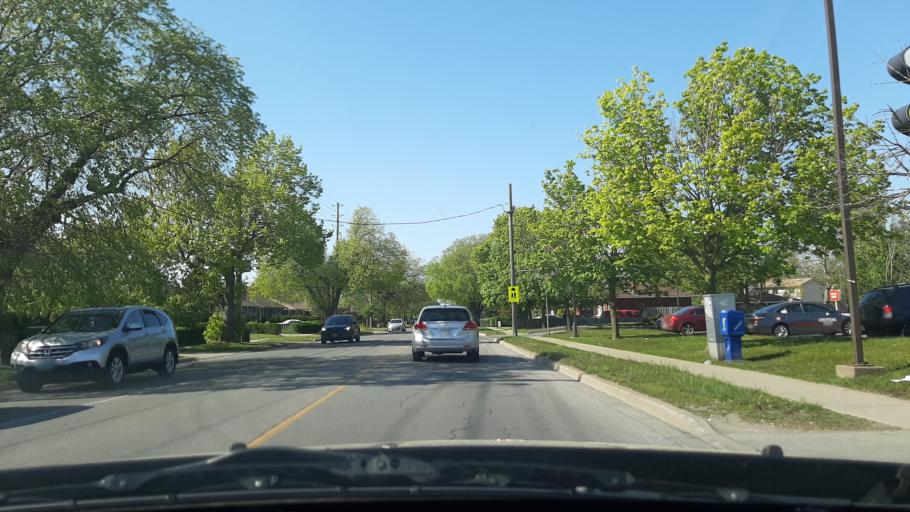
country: CA
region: Ontario
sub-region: Regional Municipality of Niagara
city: St. Catharines
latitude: 43.1862
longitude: -79.2107
